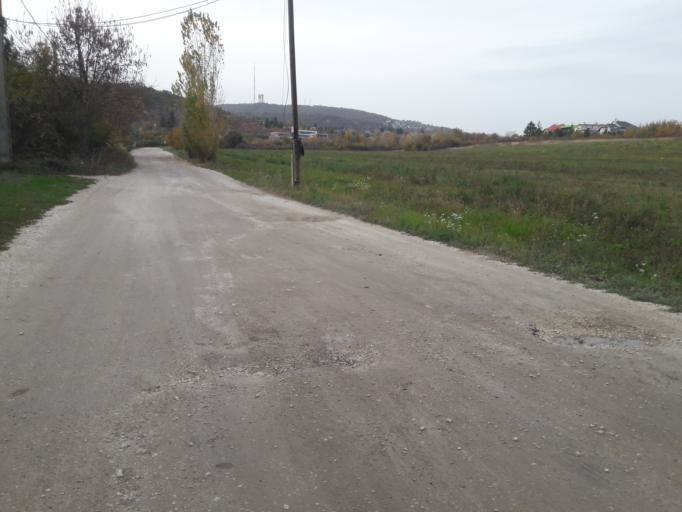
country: HU
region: Pest
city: Budaors
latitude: 47.4685
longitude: 18.9826
